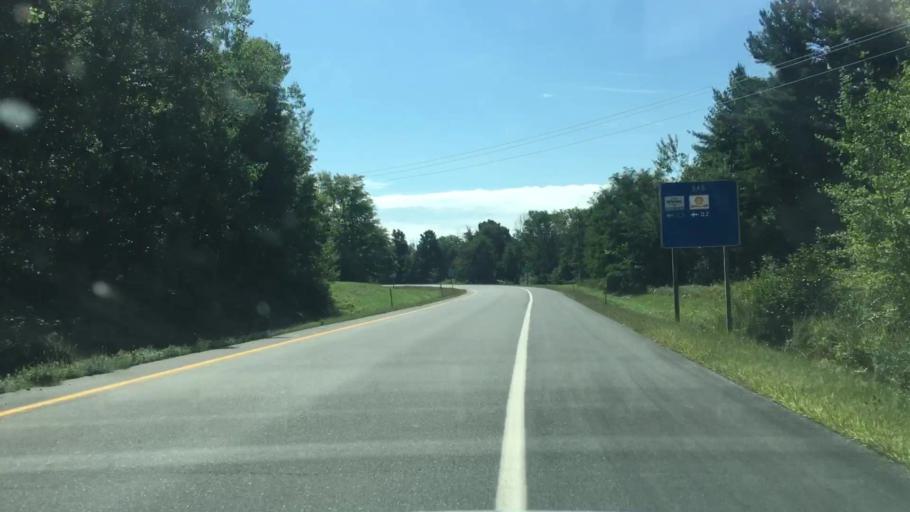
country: US
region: Maine
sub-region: Penobscot County
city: Newport
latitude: 44.8342
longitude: -69.2956
